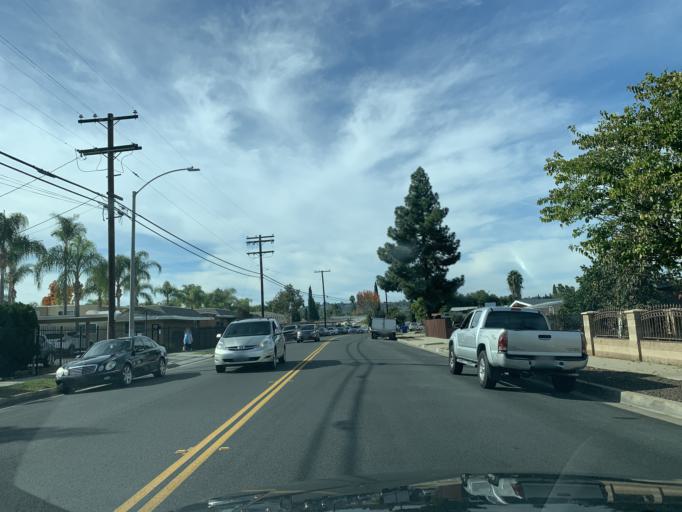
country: US
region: California
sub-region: San Diego County
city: El Cajon
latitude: 32.8006
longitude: -116.9554
